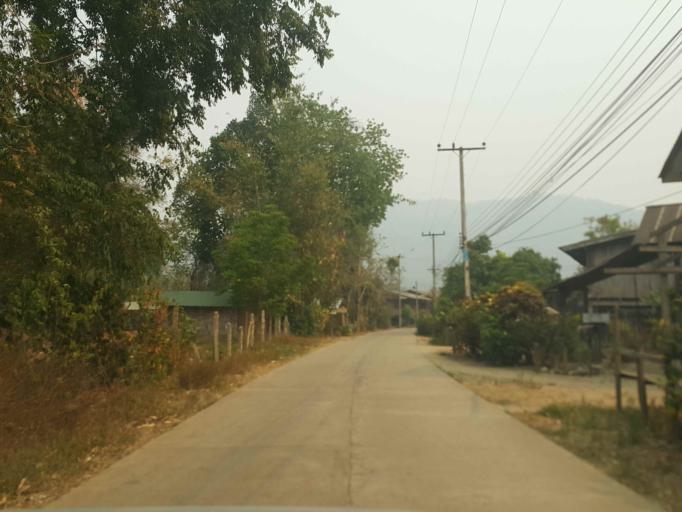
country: TH
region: Chiang Mai
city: Mae Taeng
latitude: 19.2176
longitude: 98.8532
